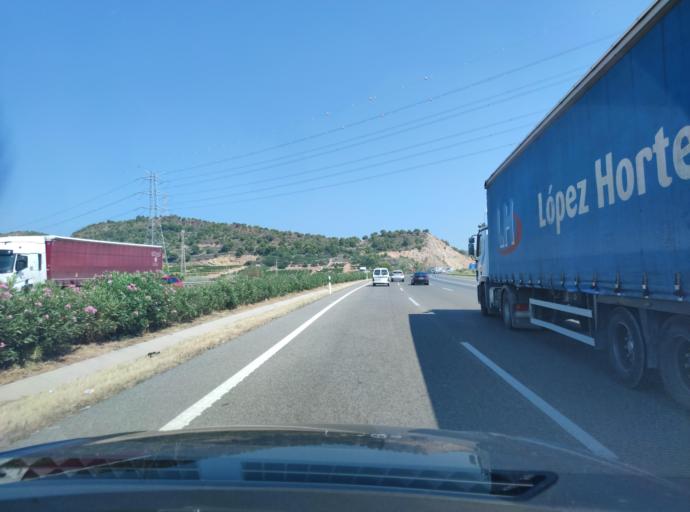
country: ES
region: Valencia
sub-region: Provincia de Valencia
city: Petres
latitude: 39.6552
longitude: -0.3047
